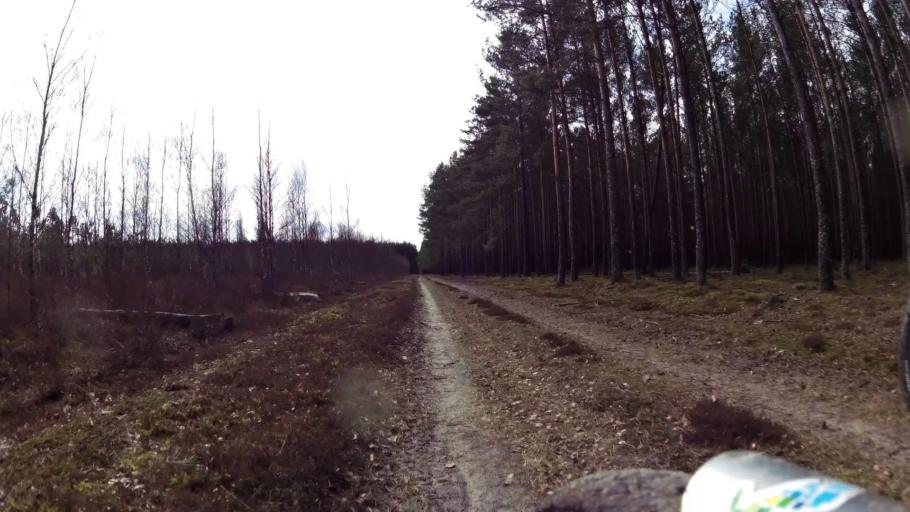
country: PL
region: Pomeranian Voivodeship
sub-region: Powiat bytowski
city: Kolczyglowy
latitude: 54.1900
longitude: 17.2137
